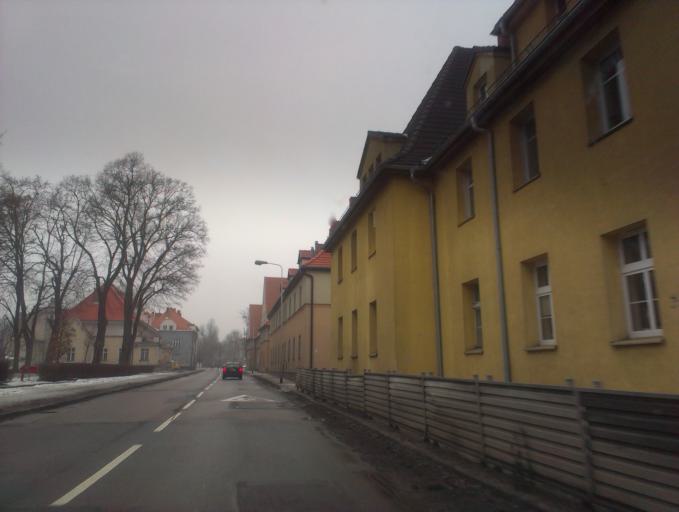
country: PL
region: Greater Poland Voivodeship
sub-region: Powiat pilski
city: Pila
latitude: 53.1539
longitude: 16.7375
